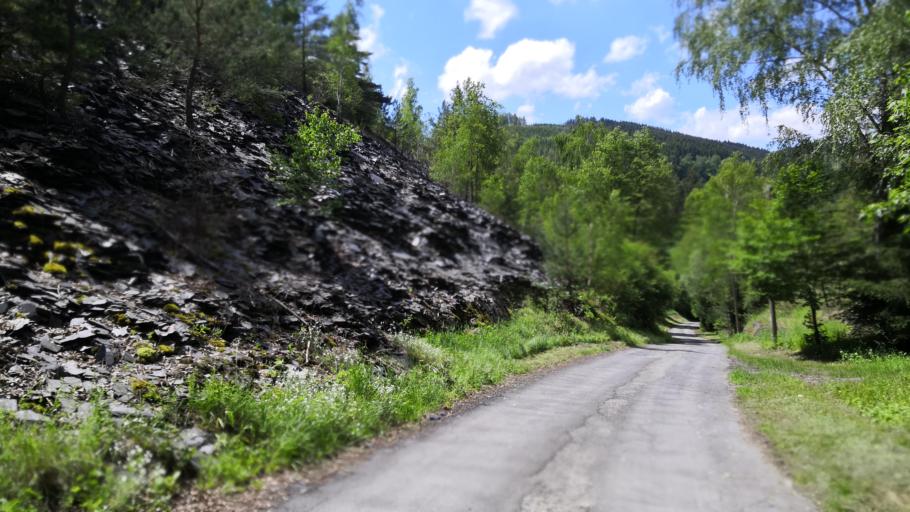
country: DE
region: Thuringia
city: Probstzella
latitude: 50.5648
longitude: 11.3846
